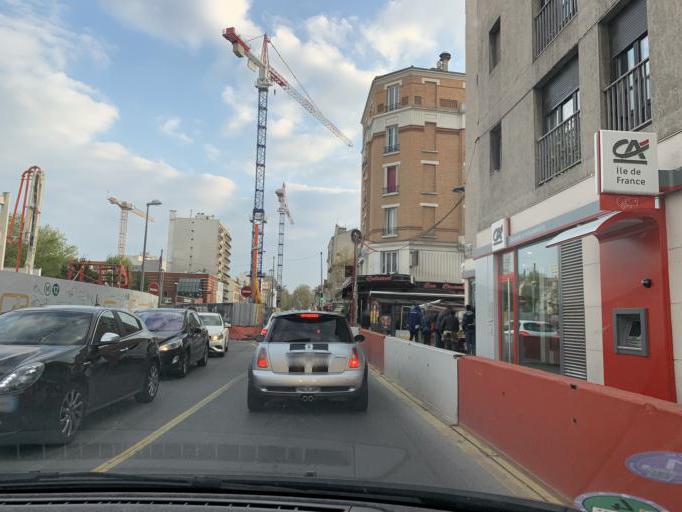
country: FR
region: Ile-de-France
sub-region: Departement de Seine-Saint-Denis
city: Aubervilliers
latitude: 48.9143
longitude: 2.3809
